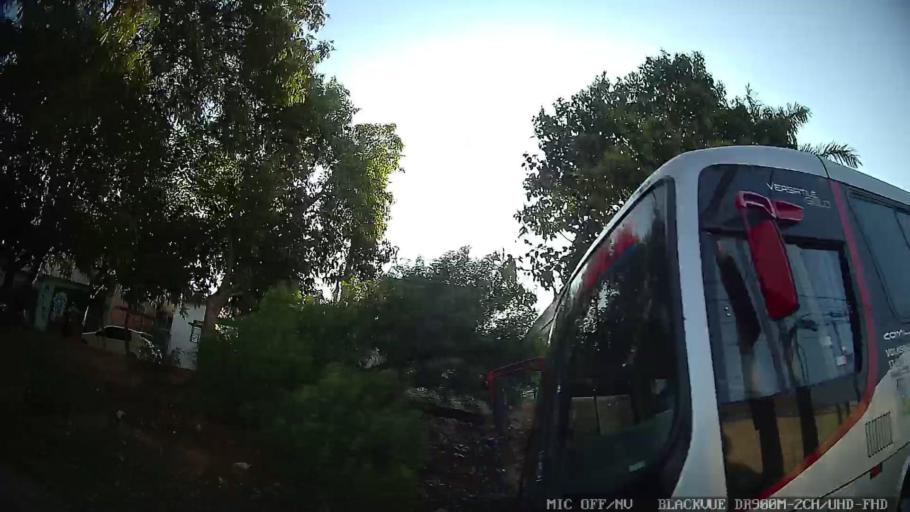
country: BR
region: Sao Paulo
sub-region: Cabreuva
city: Cabreuva
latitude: -23.2821
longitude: -47.0589
